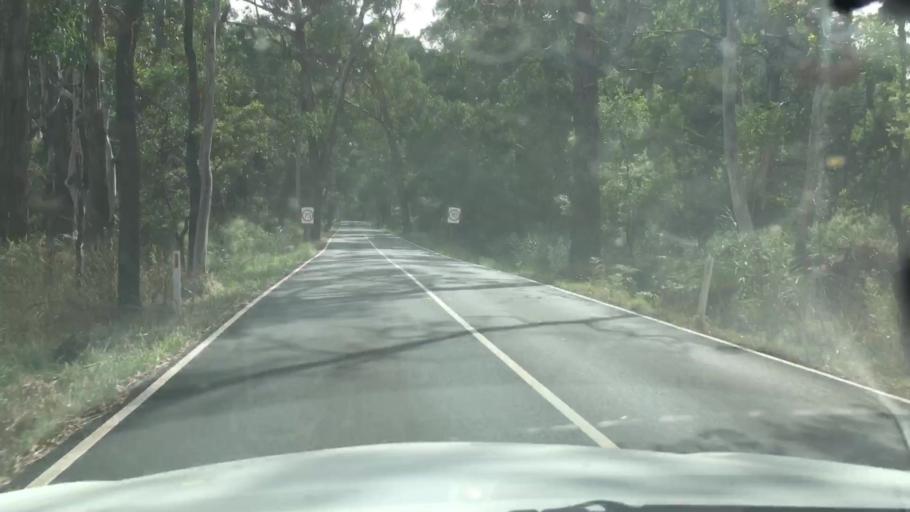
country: AU
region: Victoria
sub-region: Yarra Ranges
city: Woori Yallock
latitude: -37.8144
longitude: 145.5018
